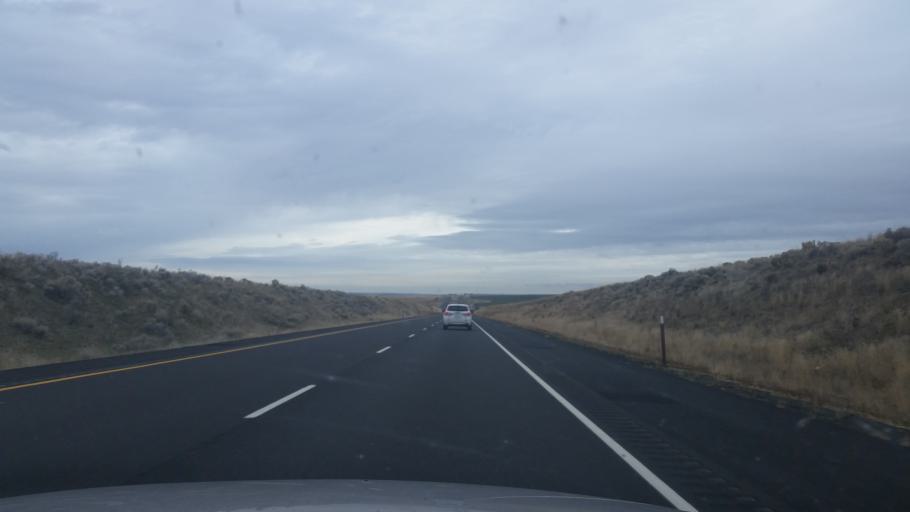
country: US
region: Washington
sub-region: Grant County
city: Warden
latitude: 47.0865
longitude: -118.7310
